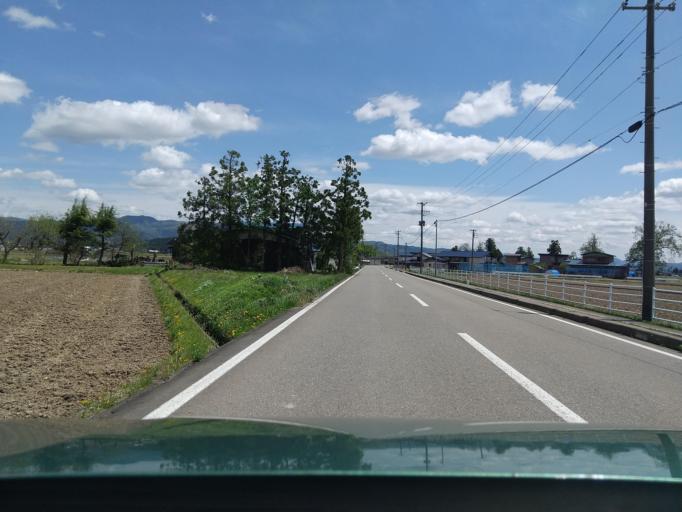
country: JP
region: Akita
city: Omagari
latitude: 39.3851
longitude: 140.5143
